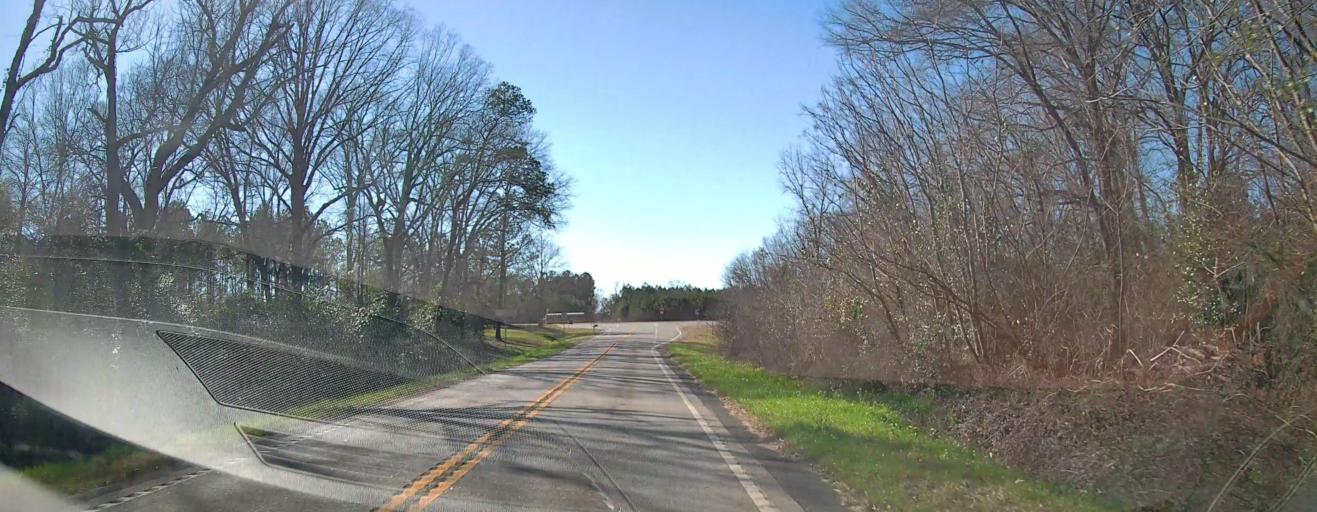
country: US
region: Georgia
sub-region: Schley County
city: Ellaville
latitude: 32.1823
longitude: -84.2658
